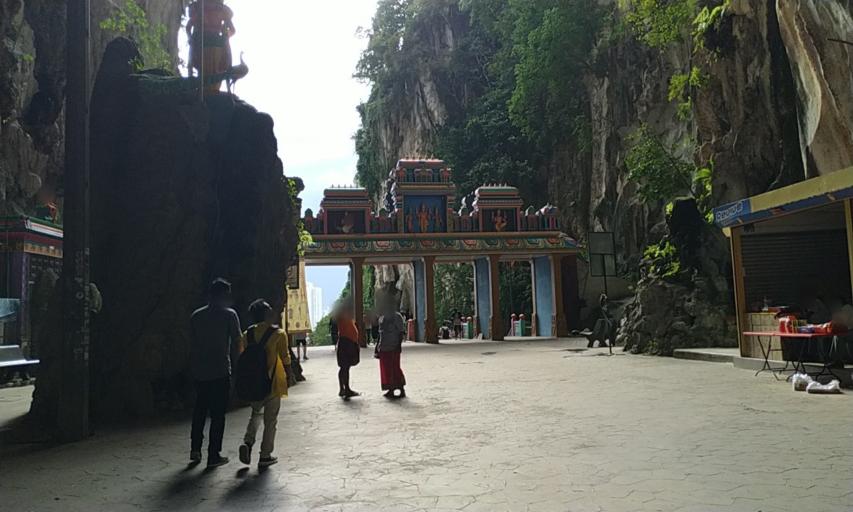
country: MY
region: Kuala Lumpur
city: Kuala Lumpur
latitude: 3.2382
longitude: 101.6846
